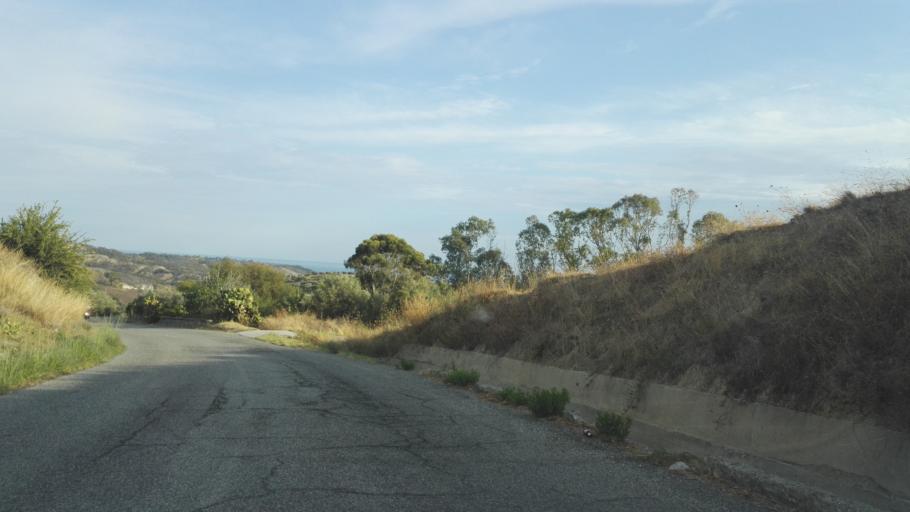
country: IT
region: Calabria
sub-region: Provincia di Reggio Calabria
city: Stignano
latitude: 38.4058
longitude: 16.4723
